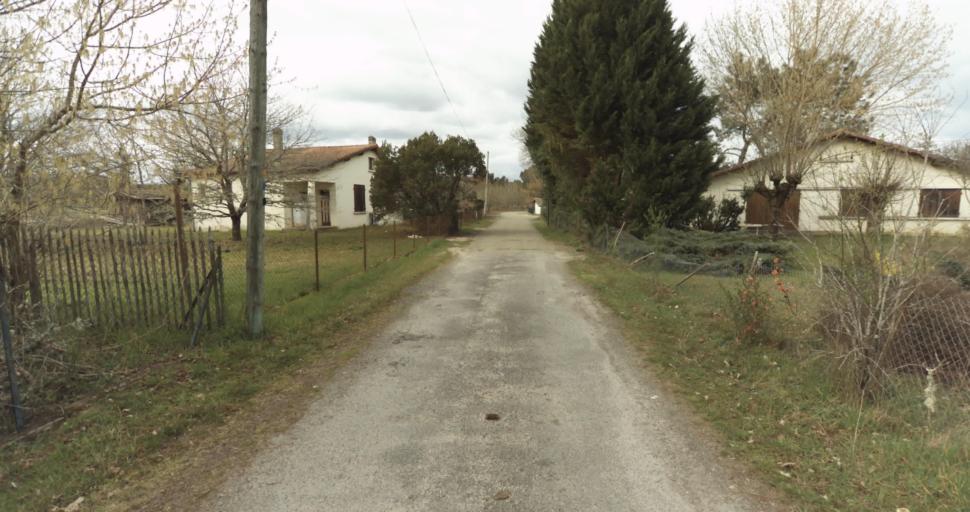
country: FR
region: Aquitaine
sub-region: Departement des Landes
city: Roquefort
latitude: 44.0482
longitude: -0.3249
